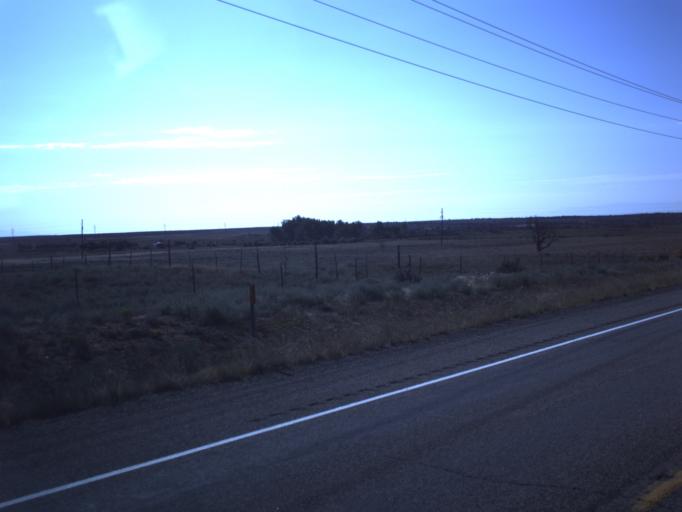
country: US
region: Utah
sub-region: San Juan County
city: Blanding
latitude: 37.5667
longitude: -109.4895
